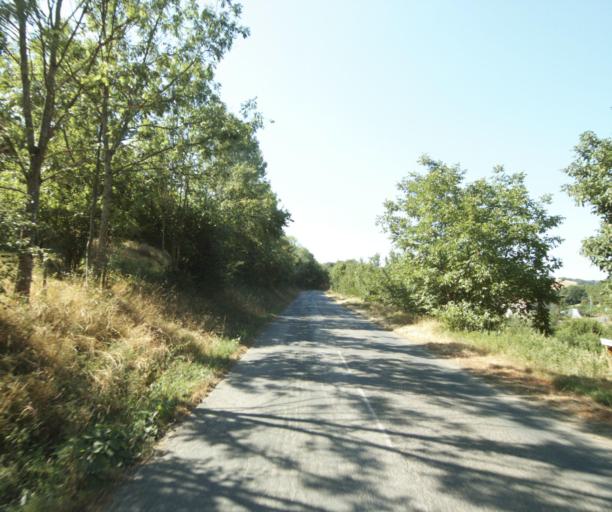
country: FR
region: Rhone-Alpes
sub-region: Departement du Rhone
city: Courzieu
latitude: 45.7486
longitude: 4.5629
